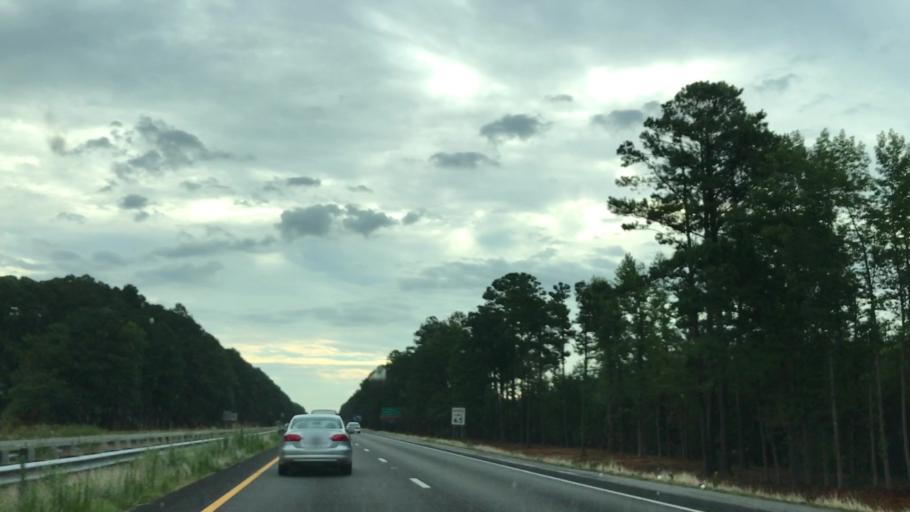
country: US
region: North Carolina
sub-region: Johnston County
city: Smithfield
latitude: 35.4950
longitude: -78.3396
